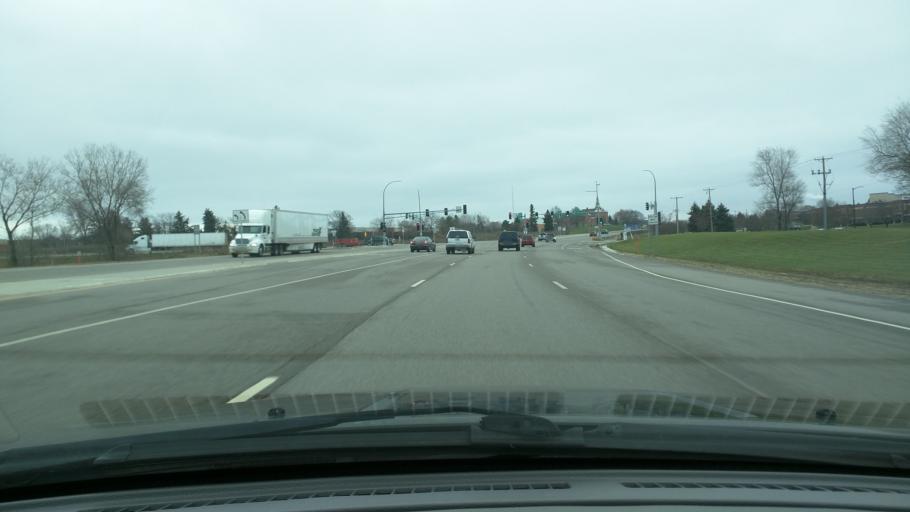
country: US
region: Minnesota
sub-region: Dakota County
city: Mendota Heights
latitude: 44.8532
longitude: -93.1315
